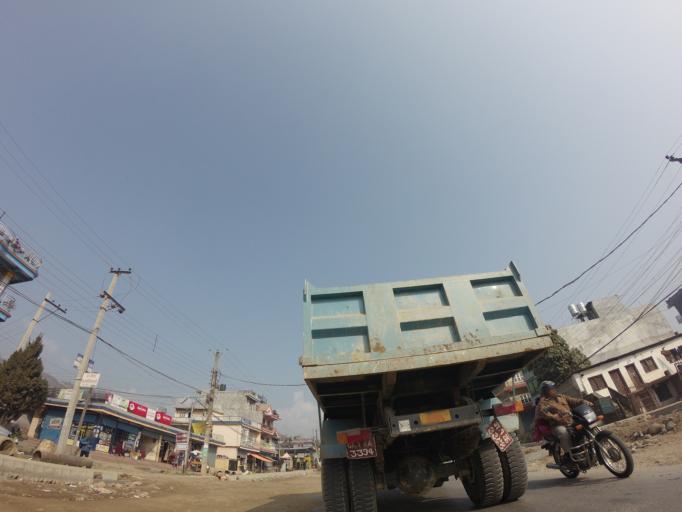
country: NP
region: Western Region
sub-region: Gandaki Zone
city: Pokhara
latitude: 28.2203
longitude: 83.9777
